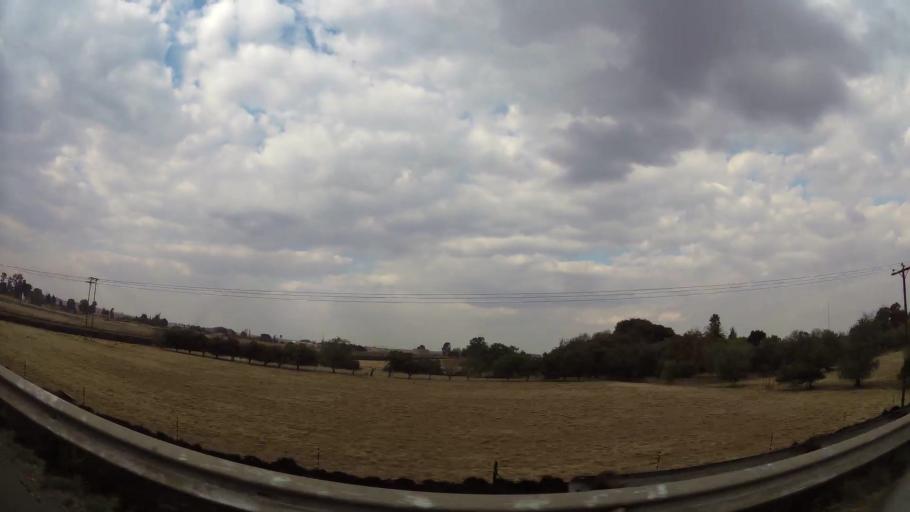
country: ZA
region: Mpumalanga
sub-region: Nkangala District Municipality
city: Delmas
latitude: -26.3047
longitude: 28.6062
